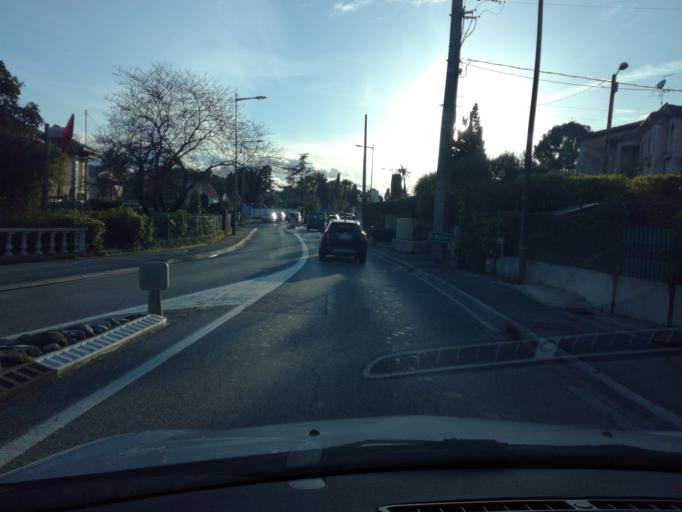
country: FR
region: Provence-Alpes-Cote d'Azur
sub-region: Departement des Alpes-Maritimes
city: Mougins
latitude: 43.6049
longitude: 7.0079
